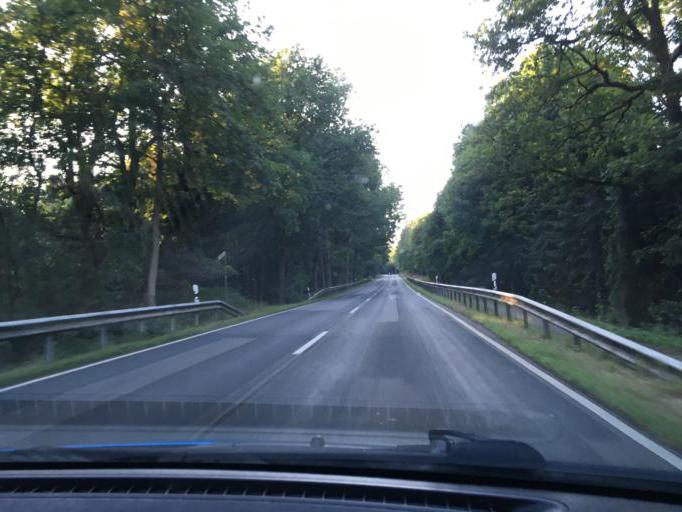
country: DE
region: Lower Saxony
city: Unterluss
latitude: 52.7982
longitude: 10.3806
